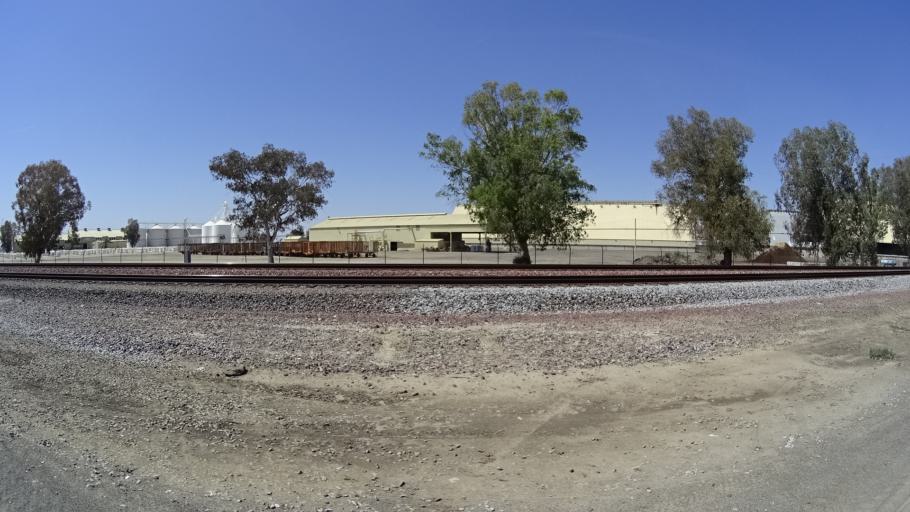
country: US
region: California
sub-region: Kings County
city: Corcoran
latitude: 36.0899
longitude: -119.5504
